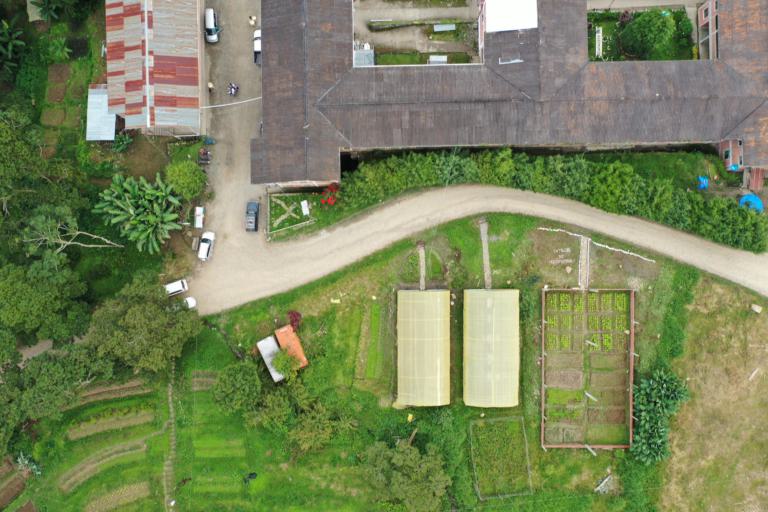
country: BO
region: La Paz
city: Coroico
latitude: -16.2582
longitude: -67.6914
